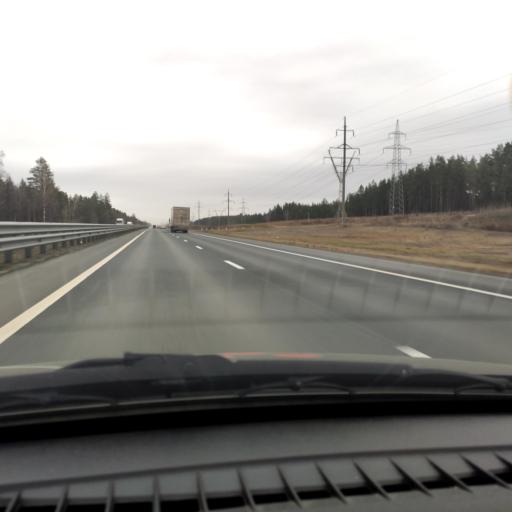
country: RU
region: Samara
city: Povolzhskiy
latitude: 53.5162
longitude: 49.7108
